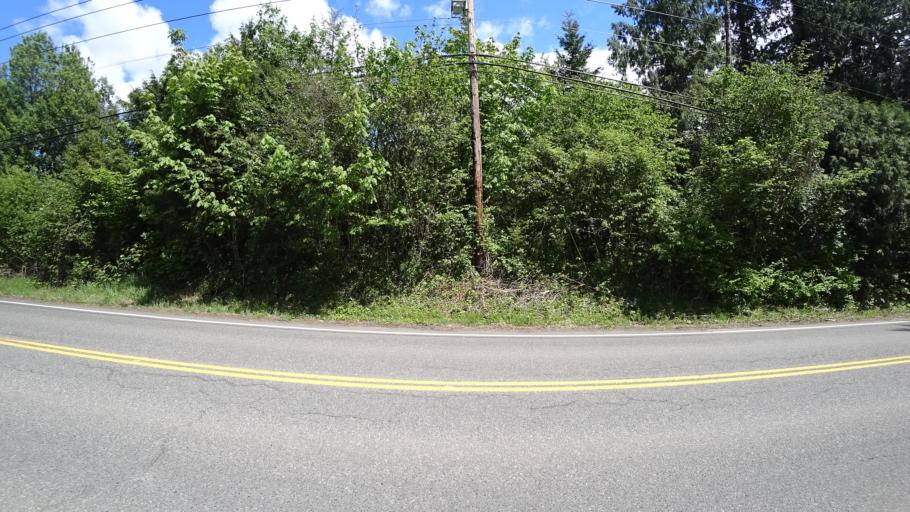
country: US
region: Oregon
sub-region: Washington County
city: West Haven
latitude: 45.5282
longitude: -122.7620
